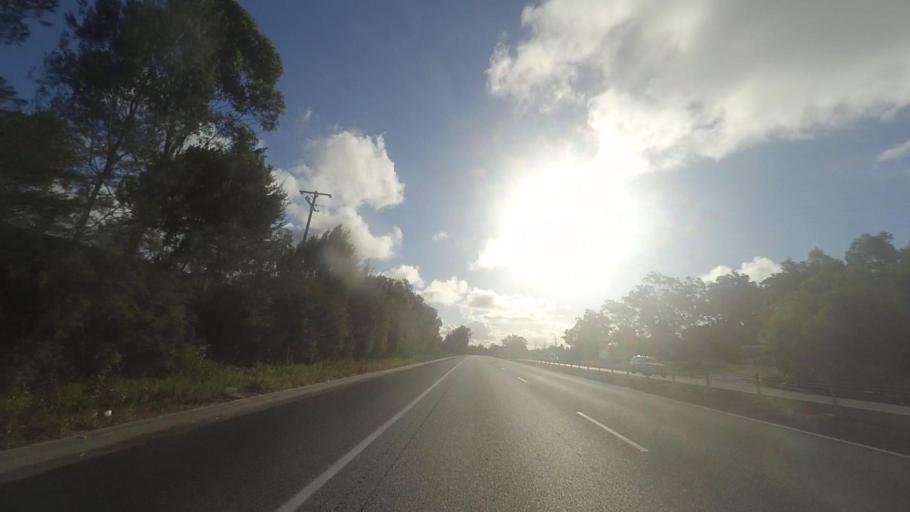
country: AU
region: New South Wales
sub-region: Great Lakes
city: Nabiac
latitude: -32.0937
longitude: 152.3841
